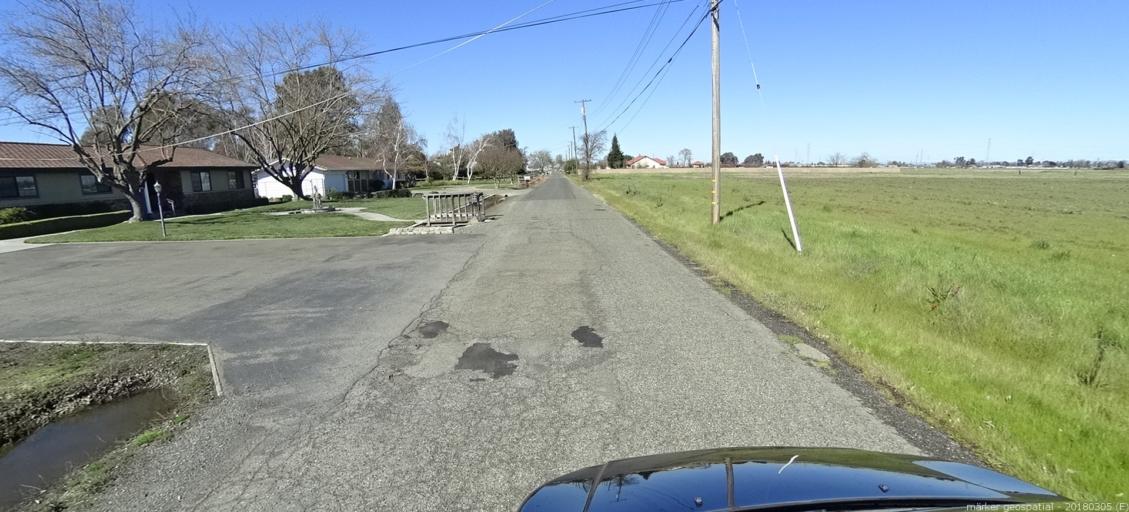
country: US
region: California
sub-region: Sacramento County
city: Florin
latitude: 38.4978
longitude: -121.3790
